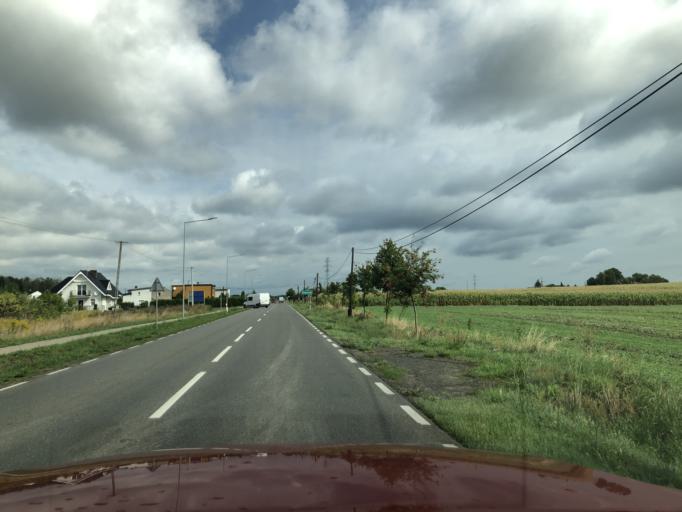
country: PL
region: Greater Poland Voivodeship
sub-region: Powiat szamotulski
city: Pniewy
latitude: 52.5248
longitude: 16.2693
